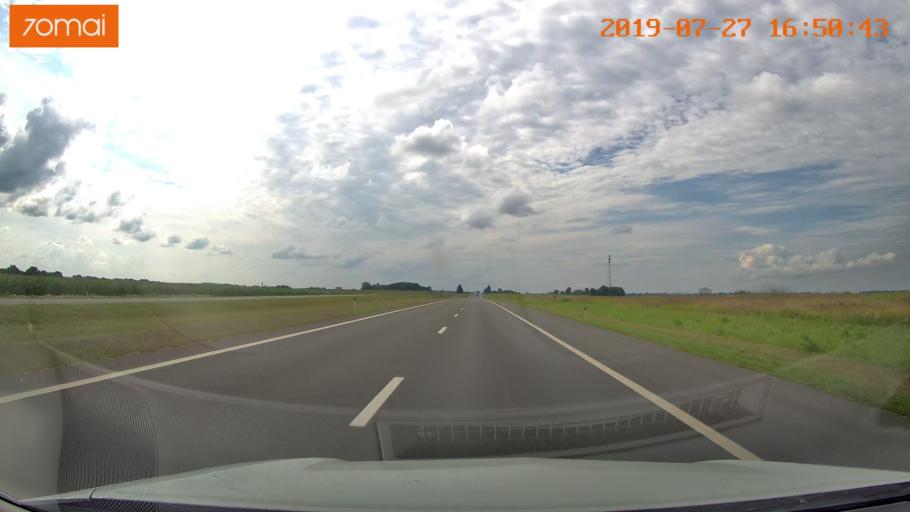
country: RU
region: Kaliningrad
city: Gvardeysk
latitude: 54.6790
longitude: 20.9061
